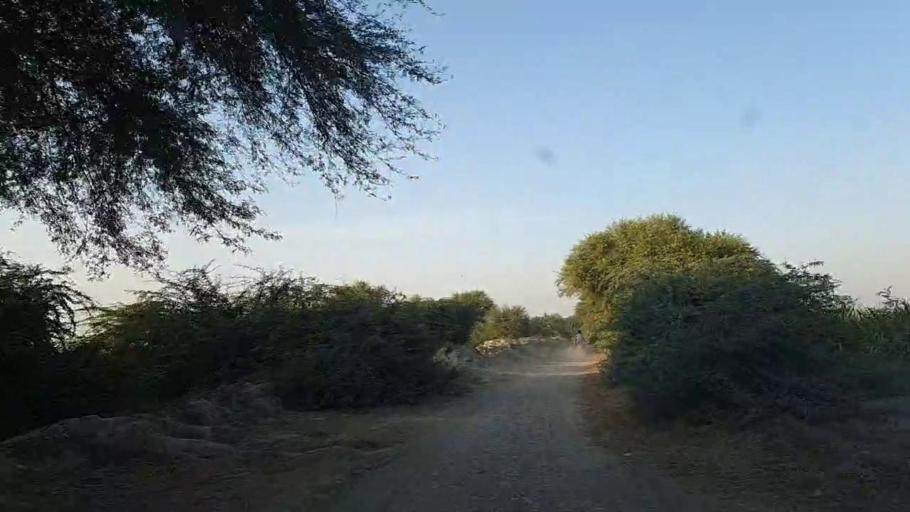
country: PK
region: Sindh
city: Mirpur Batoro
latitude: 24.7141
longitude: 68.2146
